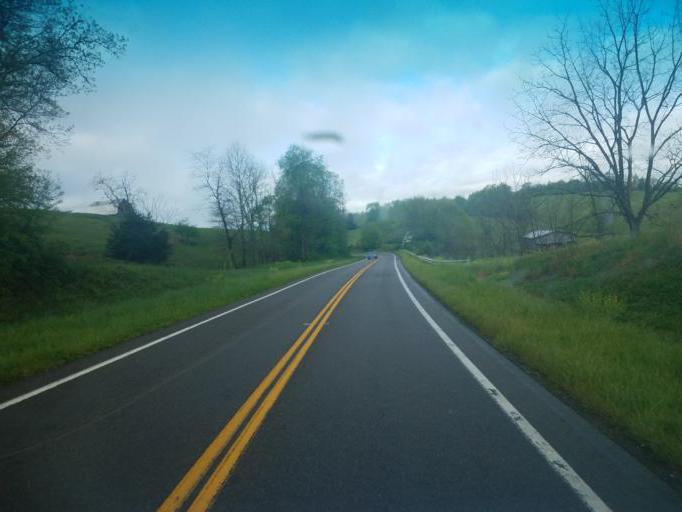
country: US
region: Virginia
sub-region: Washington County
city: Emory
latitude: 36.7003
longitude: -81.7927
